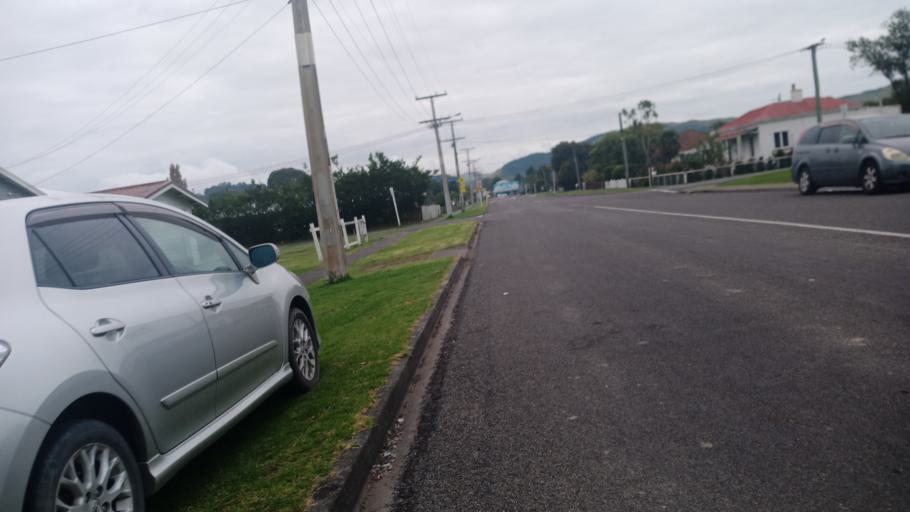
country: NZ
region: Gisborne
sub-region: Gisborne District
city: Gisborne
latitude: -38.6771
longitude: 178.0420
